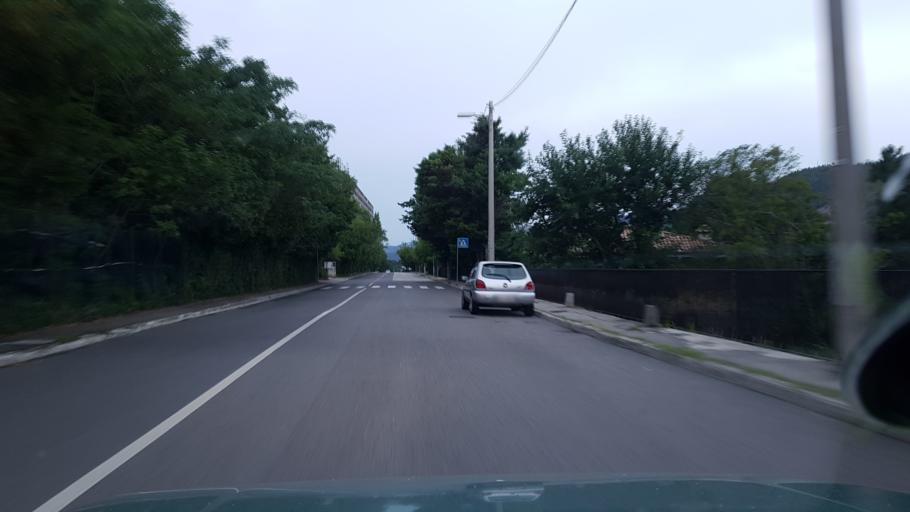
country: IT
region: Friuli Venezia Giulia
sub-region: Provincia di Trieste
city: Domio
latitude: 45.6379
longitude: 13.8294
